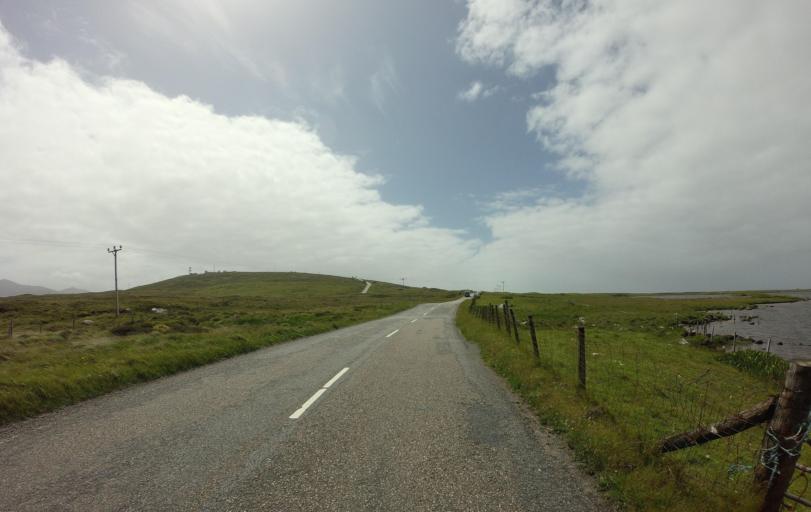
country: GB
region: Scotland
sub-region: Eilean Siar
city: Benbecula
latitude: 57.3494
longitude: -7.3582
